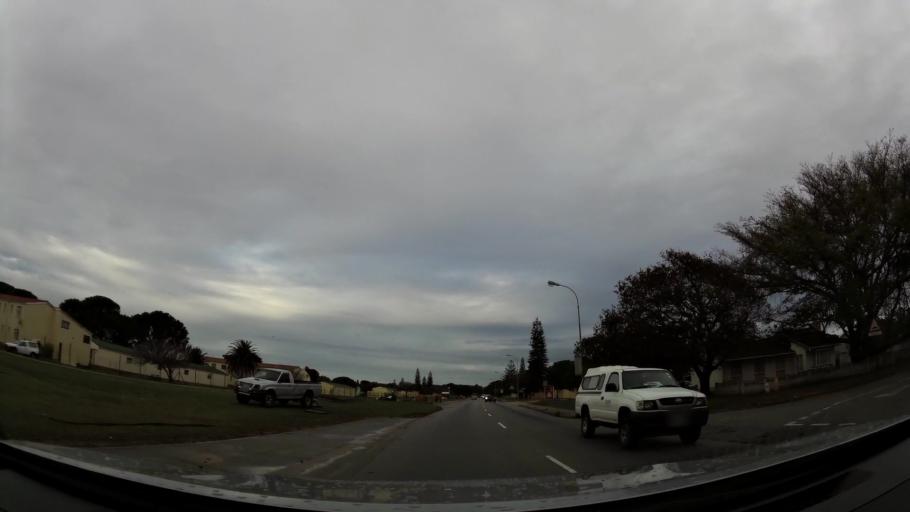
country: ZA
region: Eastern Cape
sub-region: Nelson Mandela Bay Metropolitan Municipality
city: Port Elizabeth
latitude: -33.9864
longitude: 25.5527
